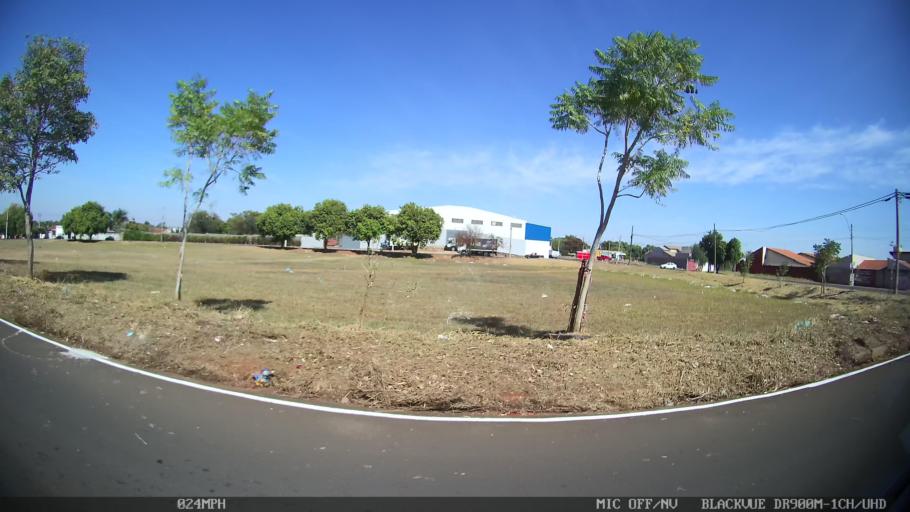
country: BR
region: Sao Paulo
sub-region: Sao Jose Do Rio Preto
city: Sao Jose do Rio Preto
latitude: -20.7723
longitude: -49.4142
